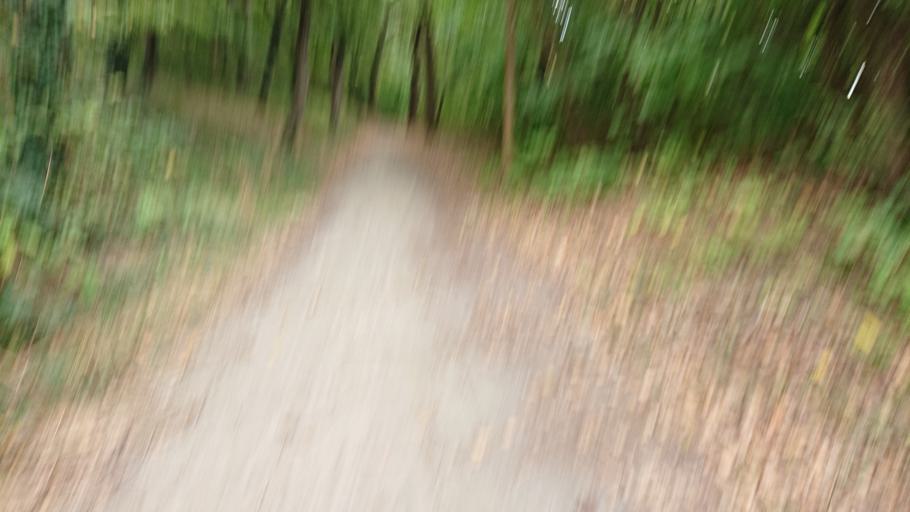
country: DE
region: Mecklenburg-Vorpommern
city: Altefahr
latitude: 54.3318
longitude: 13.1177
